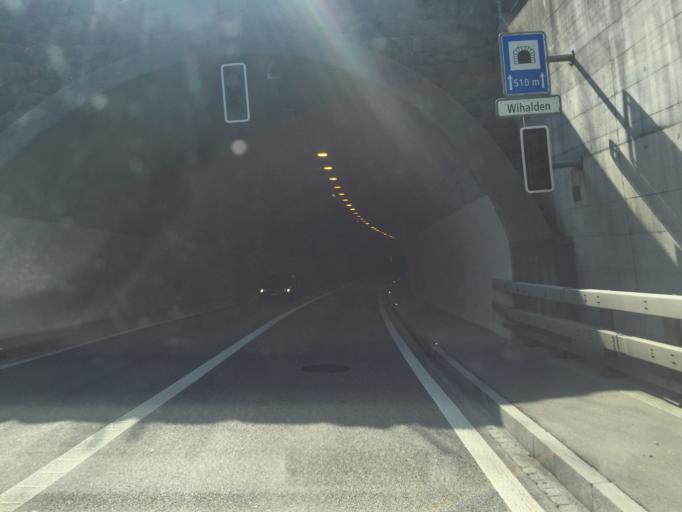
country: CH
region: Saint Gallen
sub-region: Wahlkreis Wil
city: Jonschwil
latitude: 47.4191
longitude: 9.0722
